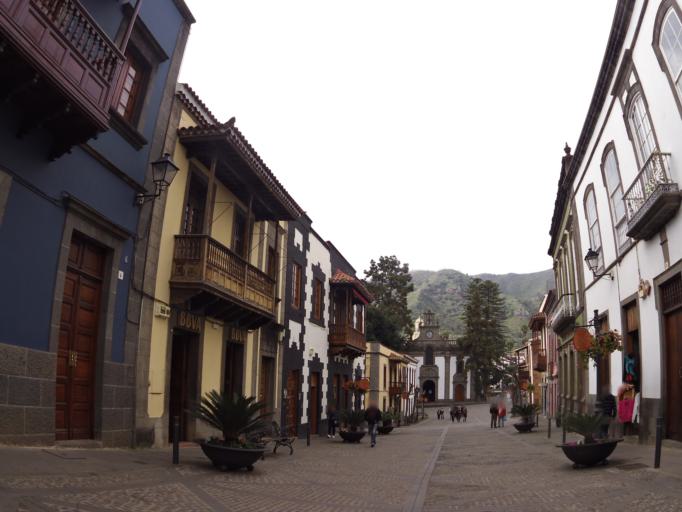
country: ES
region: Canary Islands
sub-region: Provincia de Las Palmas
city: Teror
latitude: 28.0602
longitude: -15.5469
